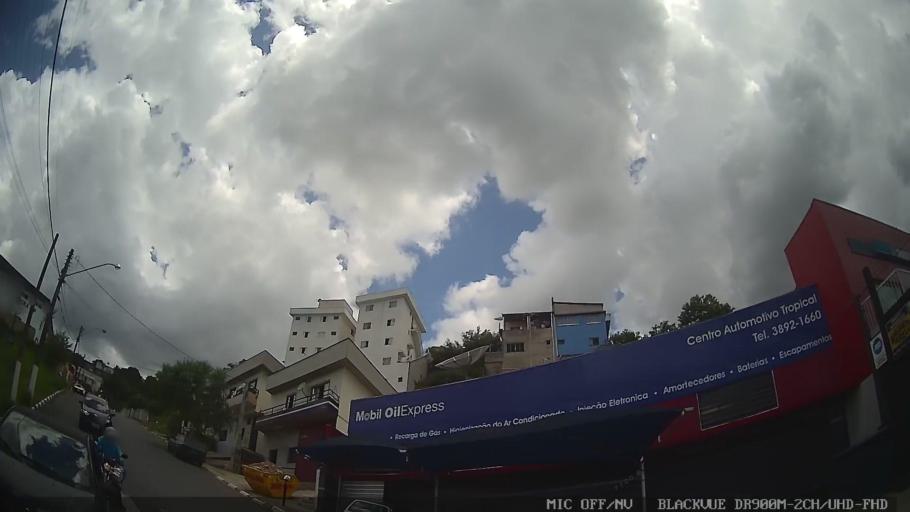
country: BR
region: Sao Paulo
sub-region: Serra Negra
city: Serra Negra
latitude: -22.5973
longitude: -46.7047
